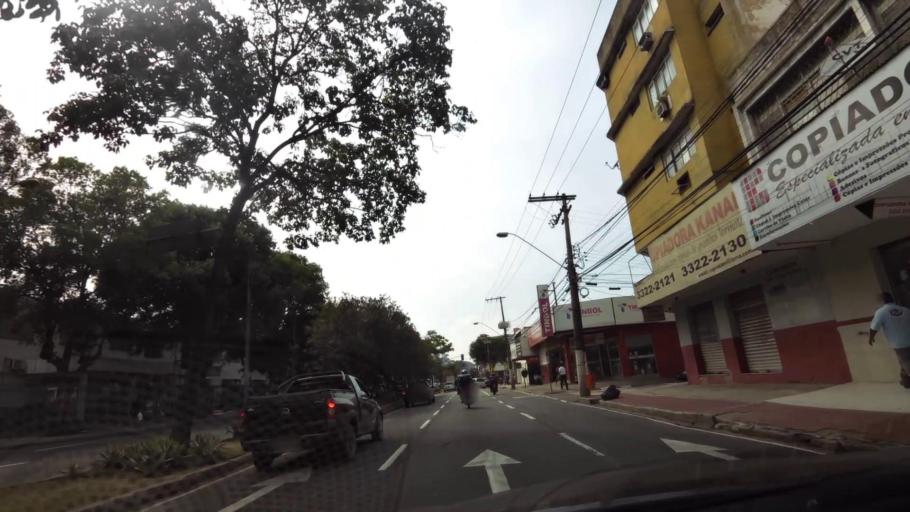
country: BR
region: Espirito Santo
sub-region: Vitoria
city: Vitoria
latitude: -20.3115
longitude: -40.3189
